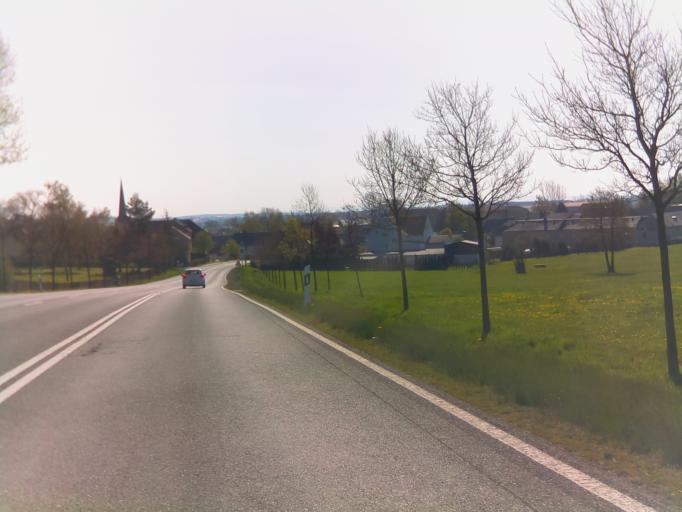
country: DE
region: Saxony
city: Muhltroff
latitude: 50.5326
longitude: 11.8873
